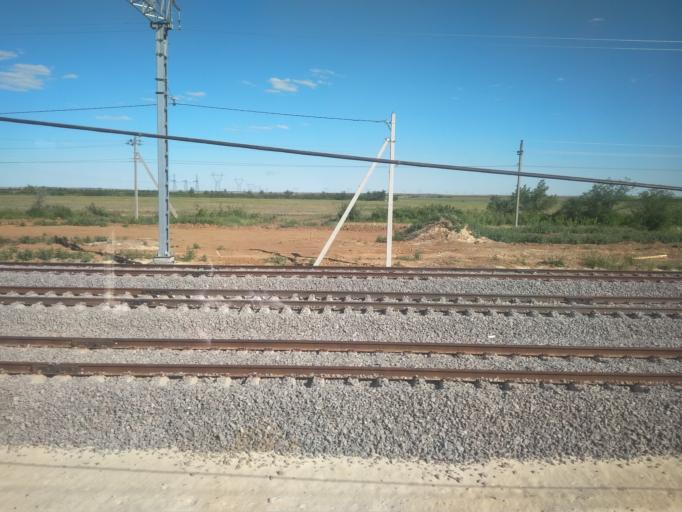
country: RU
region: Volgograd
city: Bereslavka
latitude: 48.2913
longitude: 44.2784
